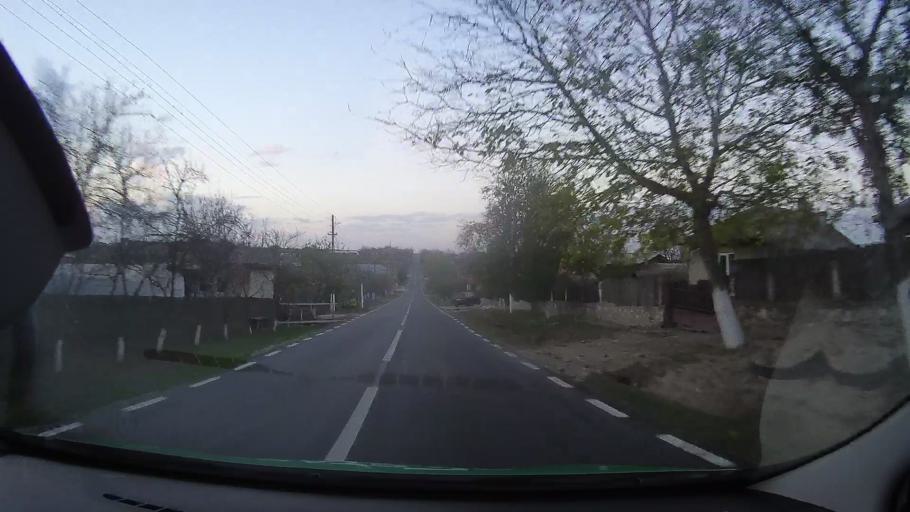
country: RO
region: Constanta
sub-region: Comuna Baneasa
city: Baneasa
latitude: 44.0982
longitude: 27.6789
